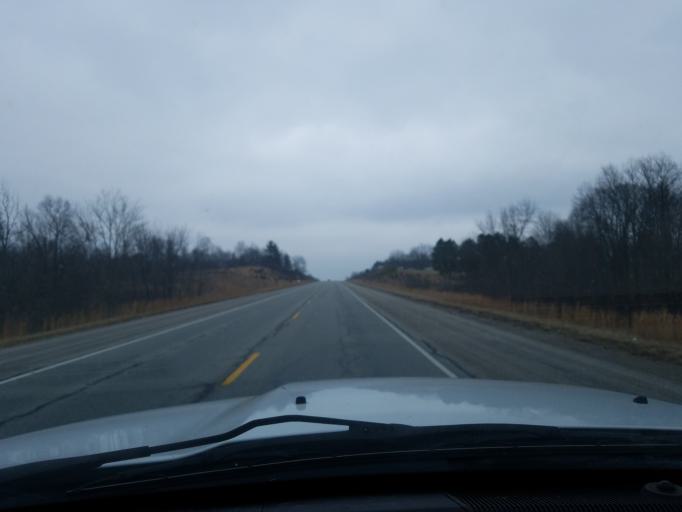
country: US
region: Indiana
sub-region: Perry County
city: Tell City
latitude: 37.9773
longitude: -86.7274
